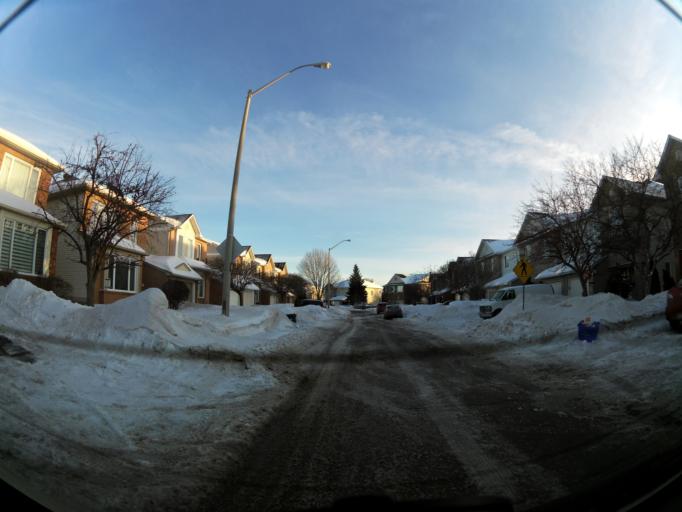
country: CA
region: Ontario
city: Ottawa
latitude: 45.4427
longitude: -75.5335
